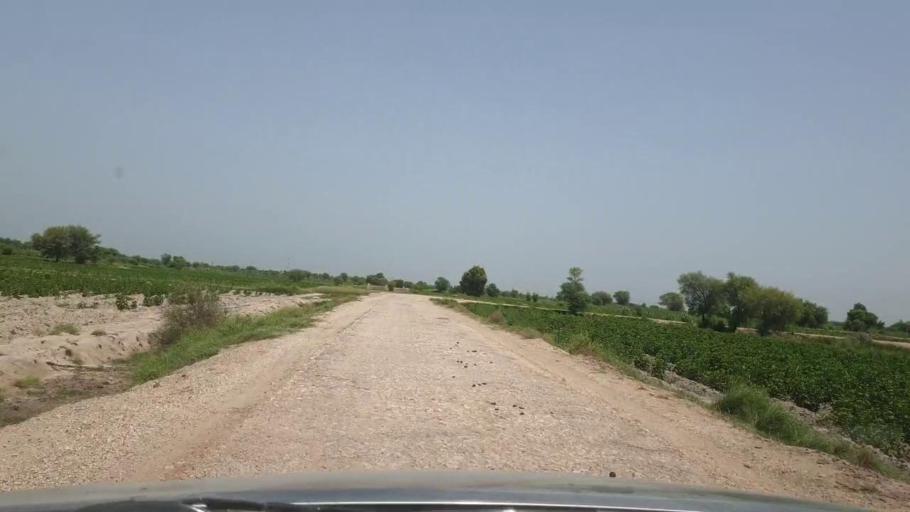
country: PK
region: Sindh
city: Pano Aqil
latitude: 27.8228
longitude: 69.2217
